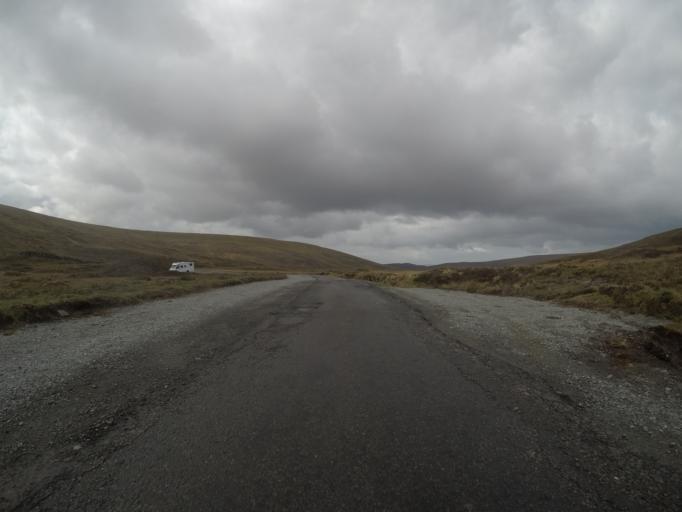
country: GB
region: Scotland
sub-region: Highland
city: Portree
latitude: 57.6280
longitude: -6.2935
